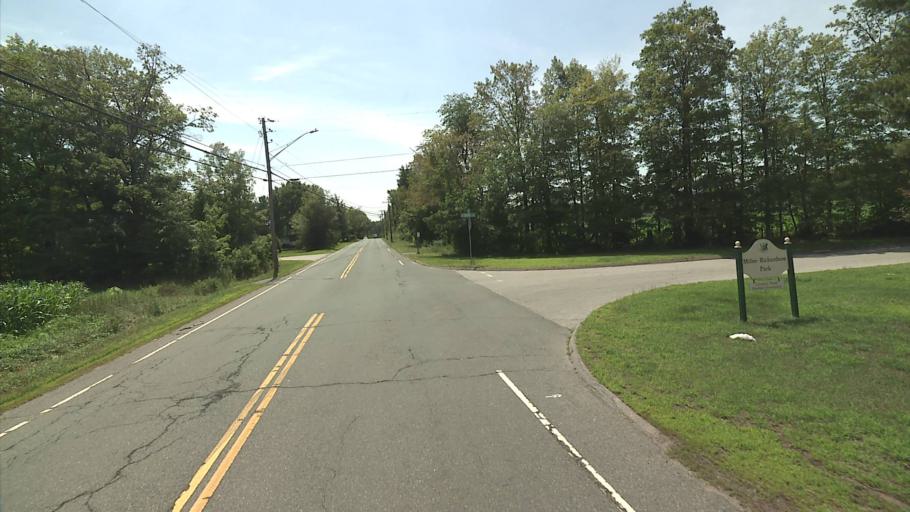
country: US
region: Connecticut
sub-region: Tolland County
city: South Coventry
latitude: 41.7537
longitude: -72.2710
